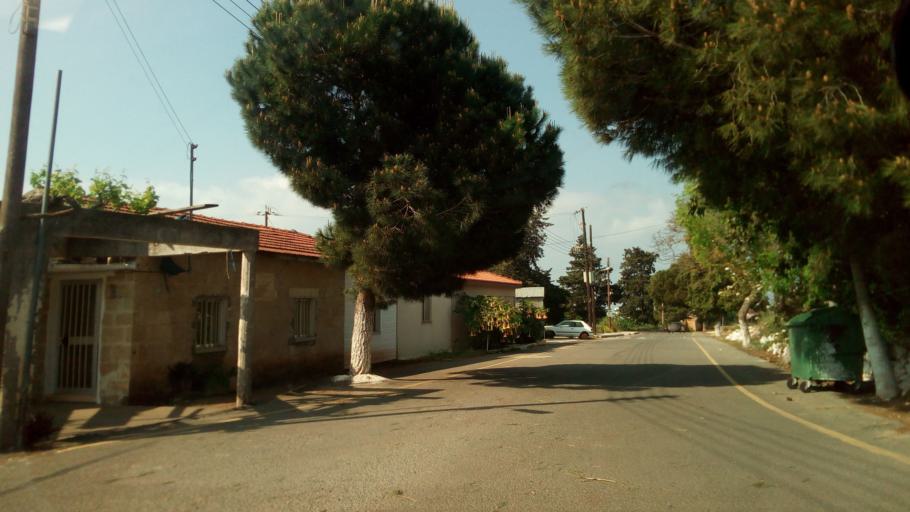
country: CY
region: Pafos
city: Pegeia
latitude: 34.9573
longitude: 32.3971
